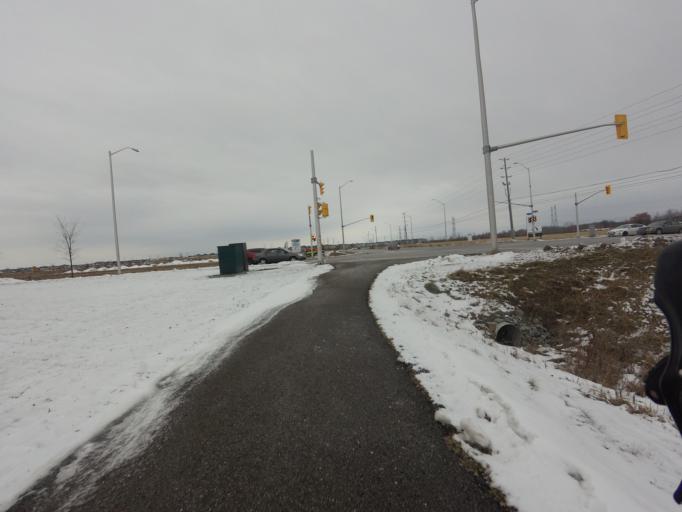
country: CA
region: Ontario
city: Bells Corners
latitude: 45.2762
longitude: -75.8727
